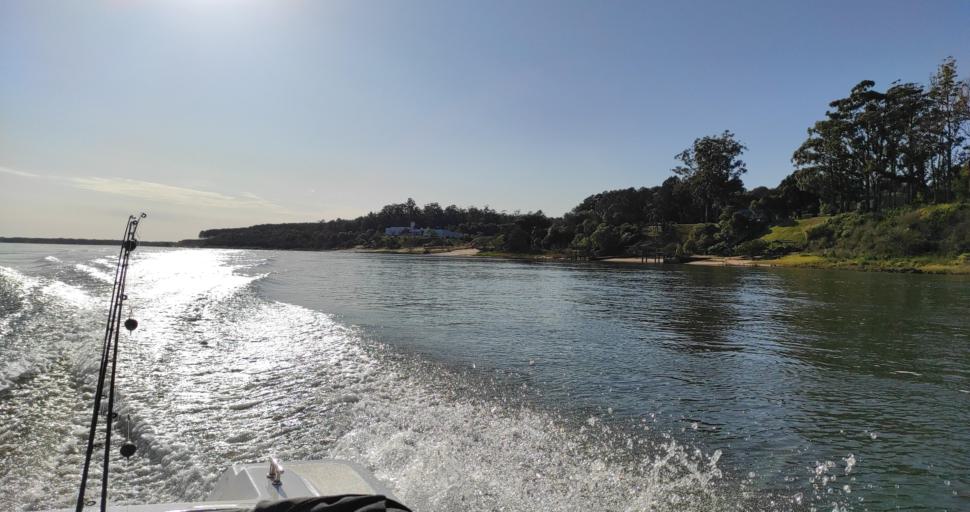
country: AR
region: Corrientes
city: Ituzaingo
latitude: -27.5946
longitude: -56.8095
